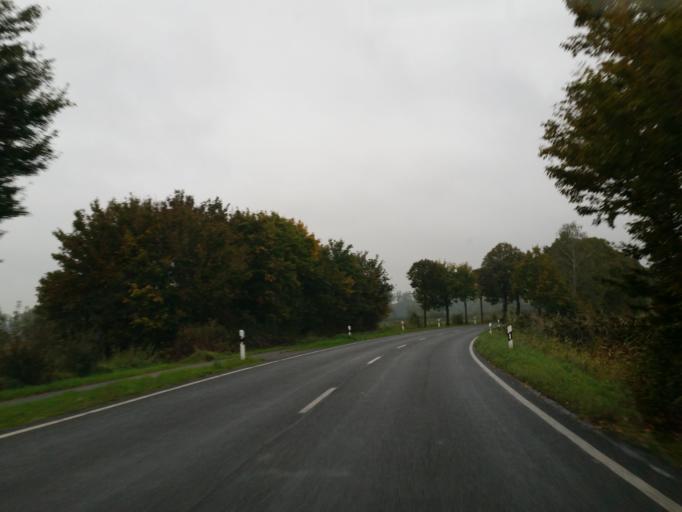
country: DE
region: Lower Saxony
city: Cremlingen
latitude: 52.2527
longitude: 10.5938
